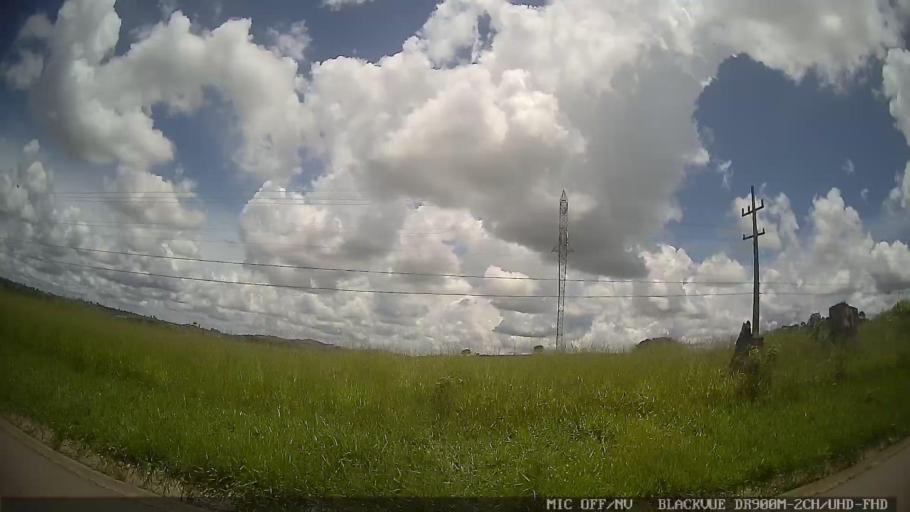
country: BR
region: Sao Paulo
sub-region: Braganca Paulista
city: Braganca Paulista
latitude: -22.8690
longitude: -46.6244
